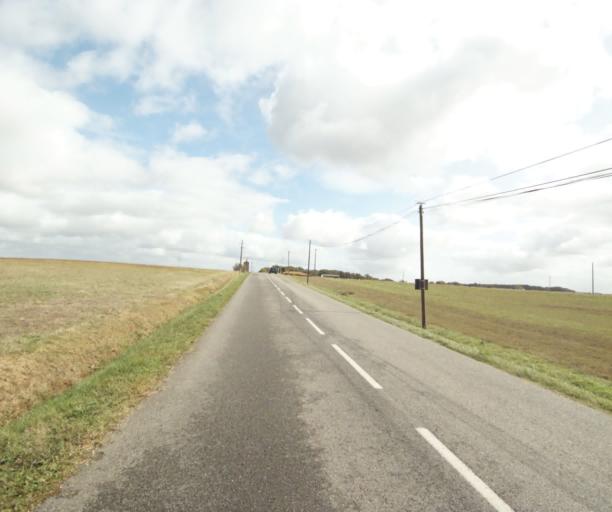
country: FR
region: Midi-Pyrenees
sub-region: Departement du Tarn-et-Garonne
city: Beaumont-de-Lomagne
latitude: 43.8645
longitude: 1.0680
